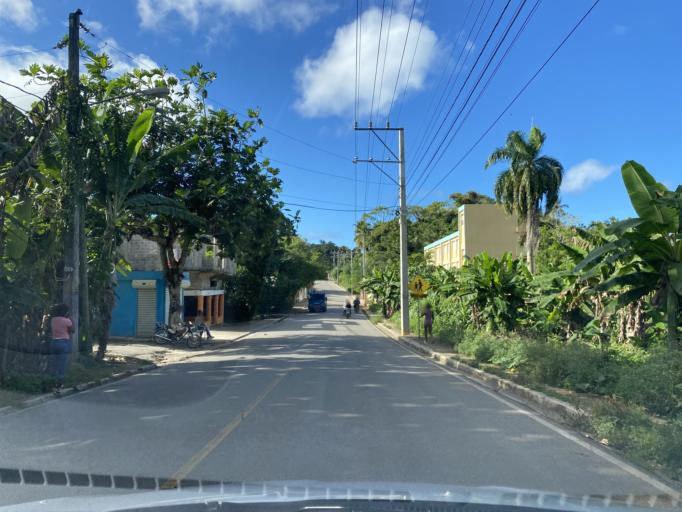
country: DO
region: Samana
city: Las Terrenas
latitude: 19.2942
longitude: -69.5481
